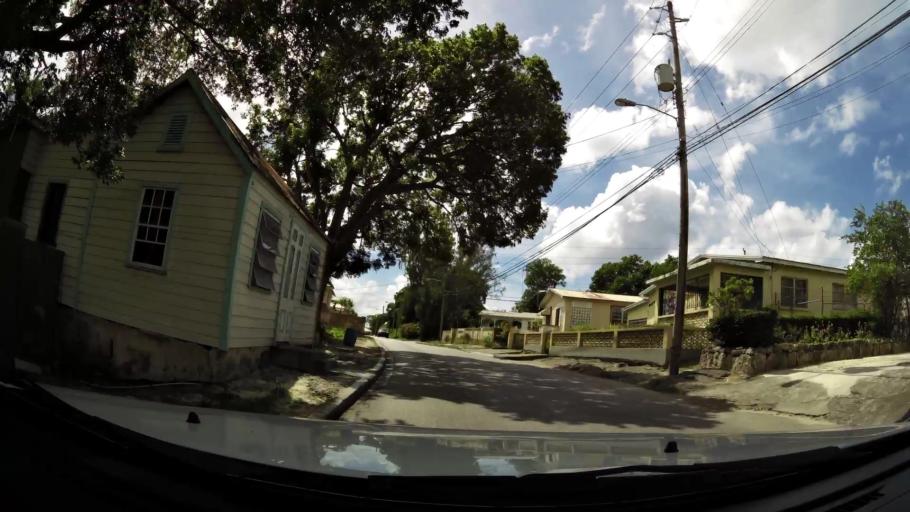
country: BB
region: Saint Michael
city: Bridgetown
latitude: 13.1274
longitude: -59.6248
